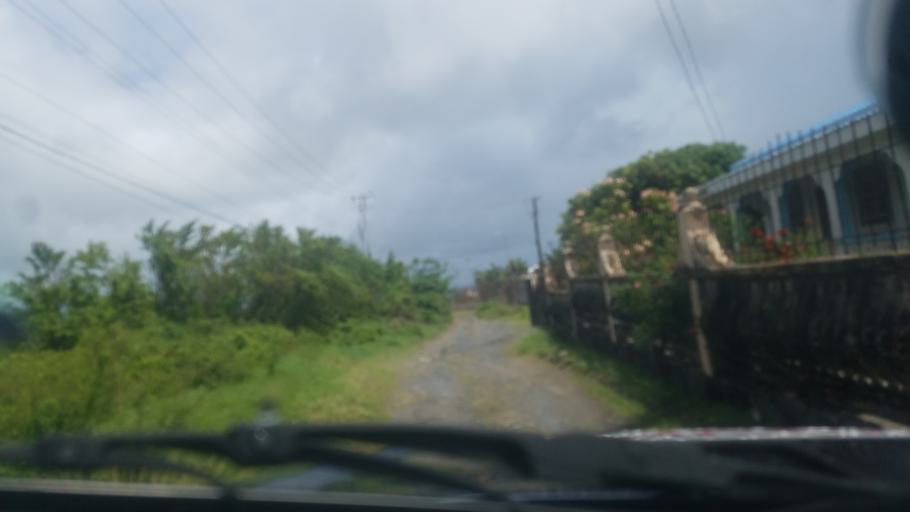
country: LC
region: Laborie Quarter
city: Laborie
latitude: 13.7530
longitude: -60.9760
